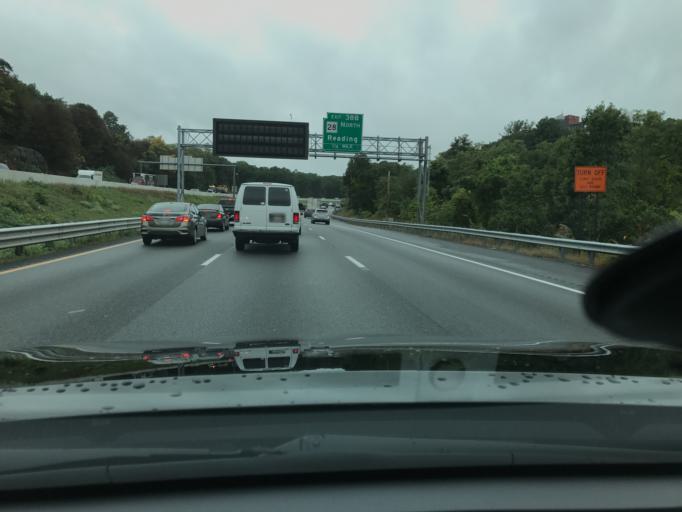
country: US
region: Massachusetts
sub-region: Middlesex County
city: Reading
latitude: 42.5090
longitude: -71.0934
